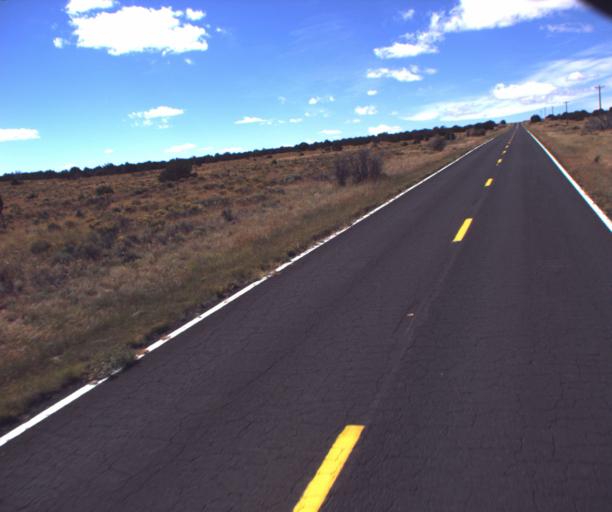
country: US
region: New Mexico
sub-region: McKinley County
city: Zuni Pueblo
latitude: 34.9900
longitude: -109.1097
